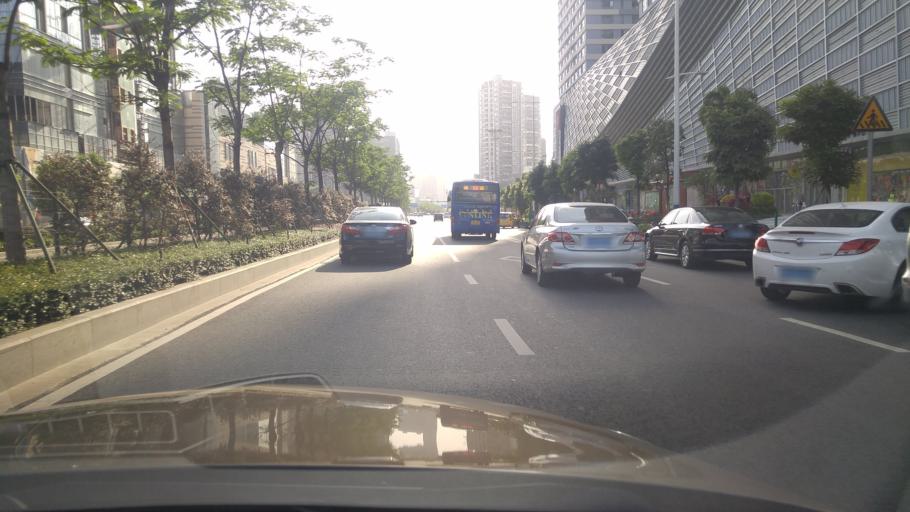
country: CN
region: Guangdong
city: Guicheng
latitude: 23.0656
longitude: 113.1526
